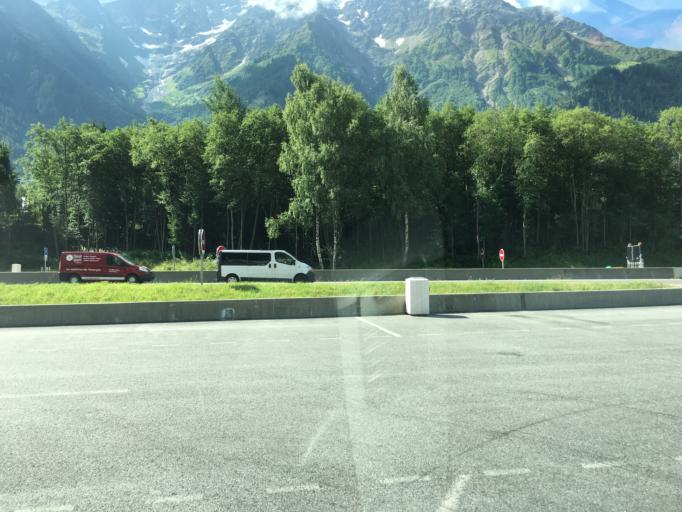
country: FR
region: Rhone-Alpes
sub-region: Departement de la Haute-Savoie
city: Les Houches
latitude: 45.8981
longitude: 6.8101
